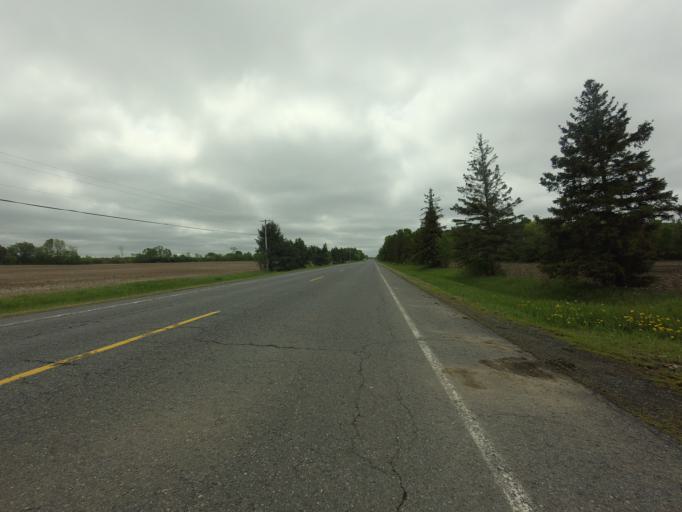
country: CA
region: Ontario
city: Casselman
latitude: 45.0425
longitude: -75.1935
